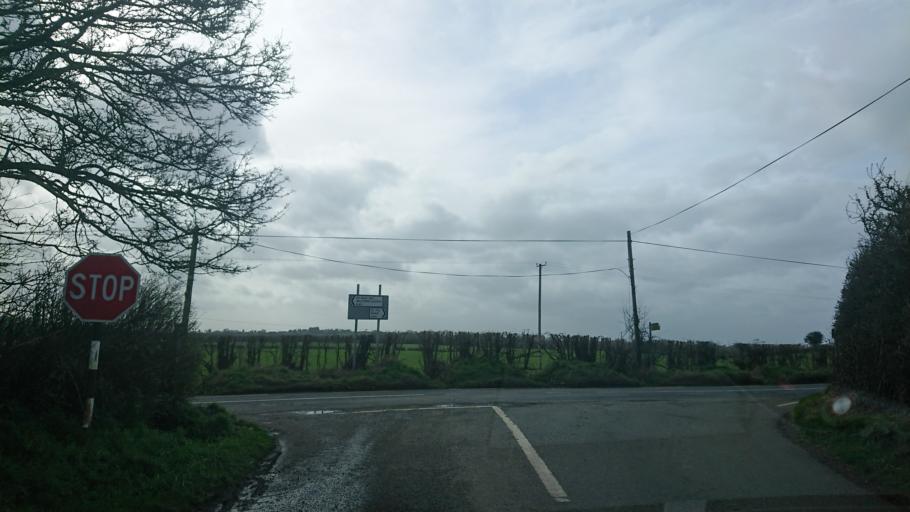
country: IE
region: Leinster
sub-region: Kildare
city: Naas
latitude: 53.1738
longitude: -6.6353
